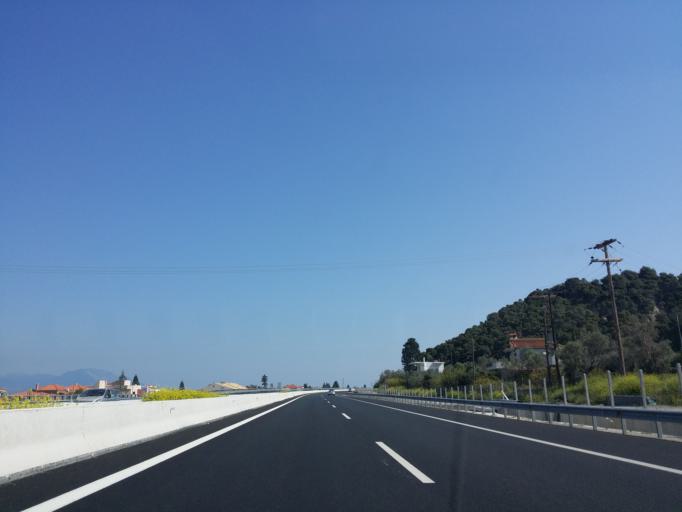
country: GR
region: Peloponnese
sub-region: Nomos Korinthias
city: Kato Dhiminio
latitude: 38.0420
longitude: 22.7035
